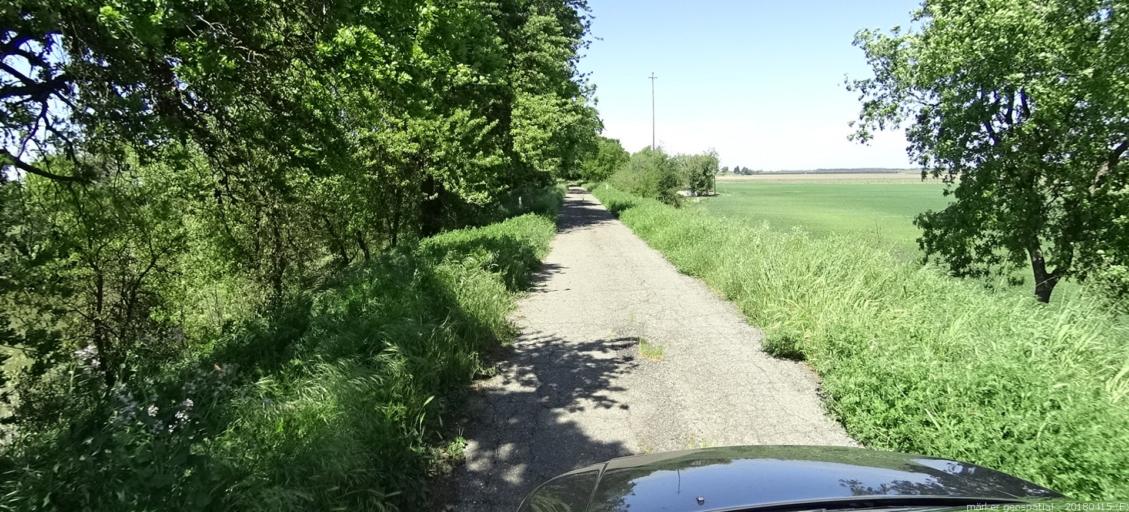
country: US
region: California
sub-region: Sacramento County
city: Walnut Grove
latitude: 38.2645
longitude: -121.6013
